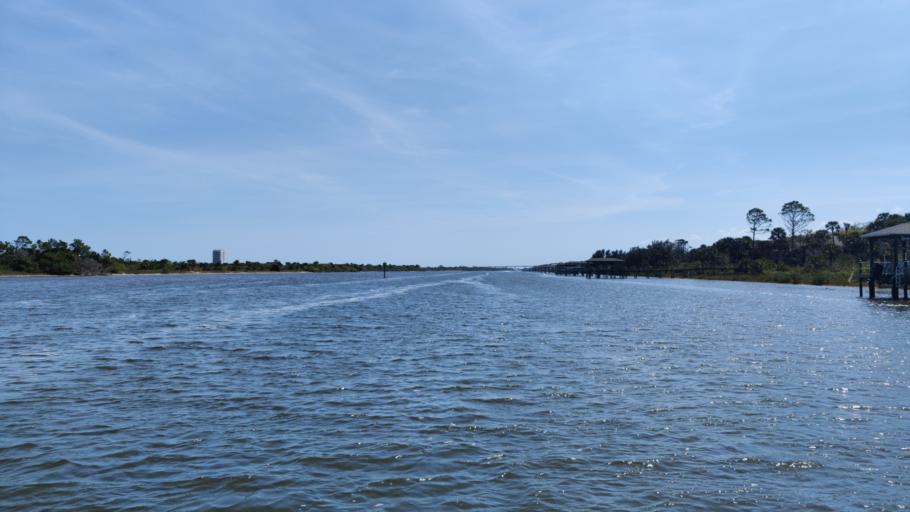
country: US
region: Florida
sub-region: Flagler County
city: Flagler Beach
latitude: 29.5068
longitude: -81.1467
